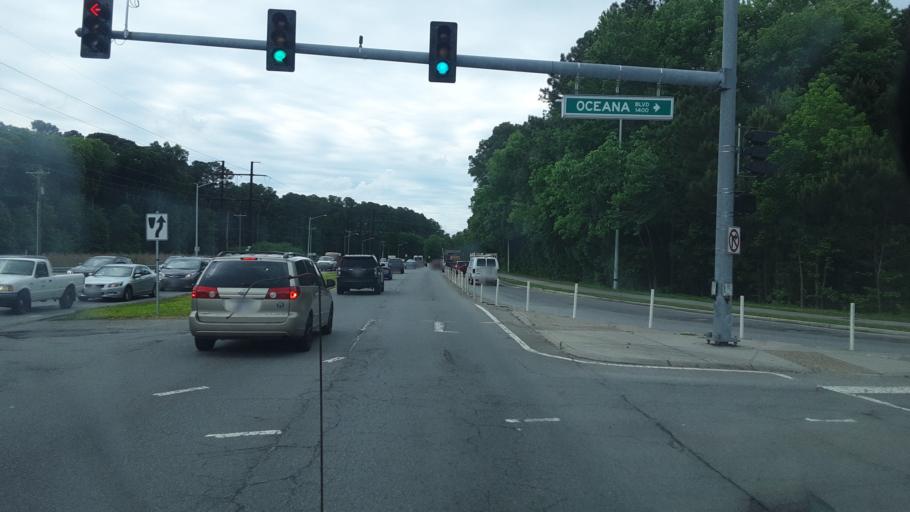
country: US
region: Virginia
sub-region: City of Virginia Beach
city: Virginia Beach
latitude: 36.7939
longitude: -75.9955
